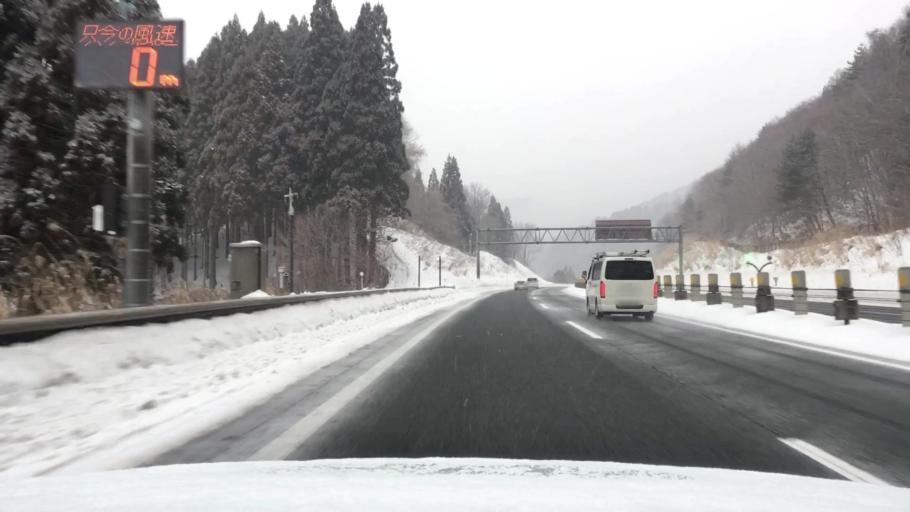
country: JP
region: Akita
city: Hanawa
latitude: 40.1116
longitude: 141.0361
